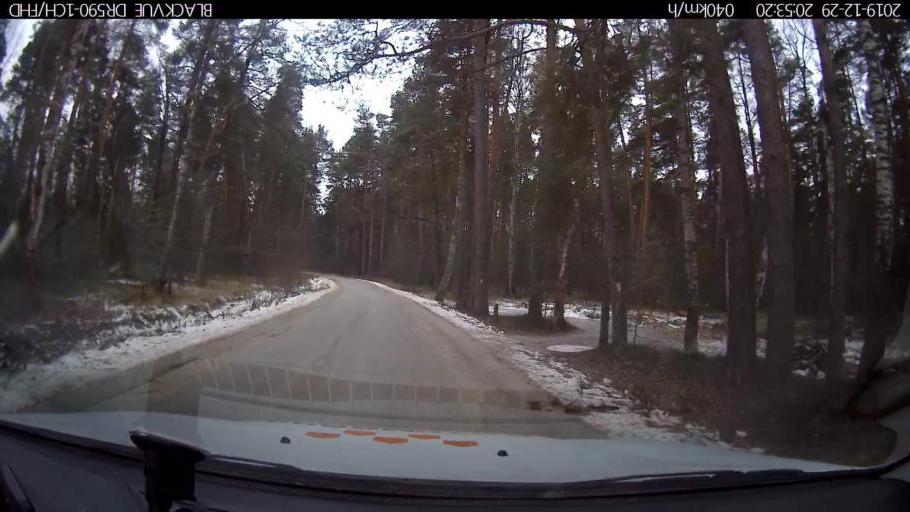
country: RU
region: Nizjnij Novgorod
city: Afonino
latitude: 56.1718
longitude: 43.9868
